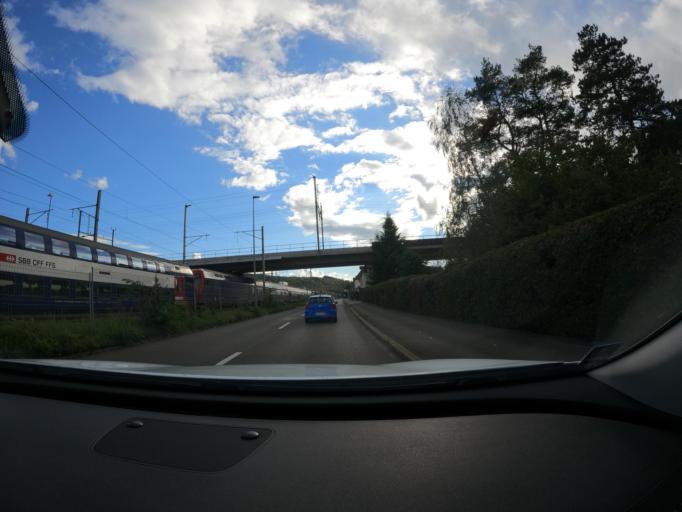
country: CH
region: Aargau
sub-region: Bezirk Brugg
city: Brugg
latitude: 47.4758
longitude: 8.2017
